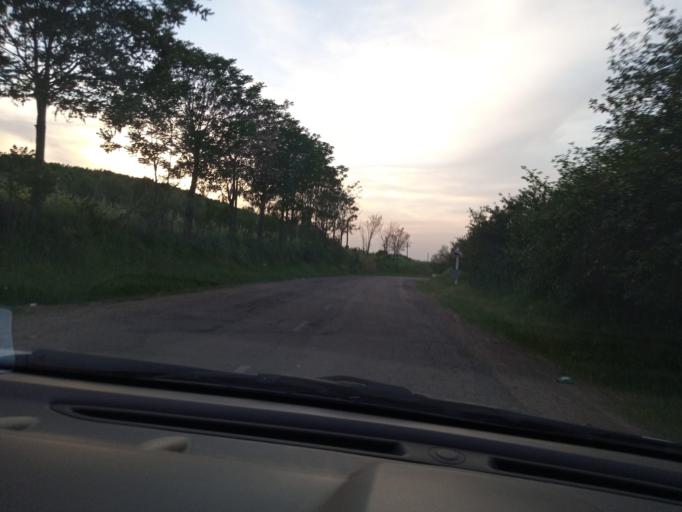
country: UZ
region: Toshkent
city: Parkent
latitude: 41.2371
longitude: 69.7354
